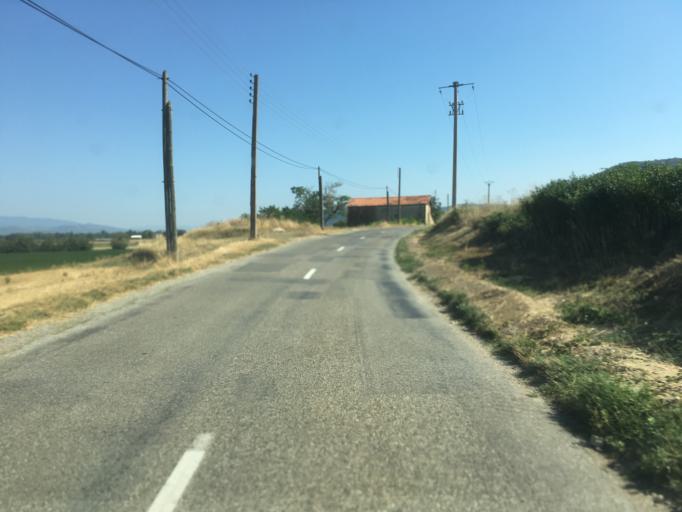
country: FR
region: Provence-Alpes-Cote d'Azur
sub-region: Departement des Alpes-de-Haute-Provence
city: Villeneuve
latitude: 43.8637
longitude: 5.8941
